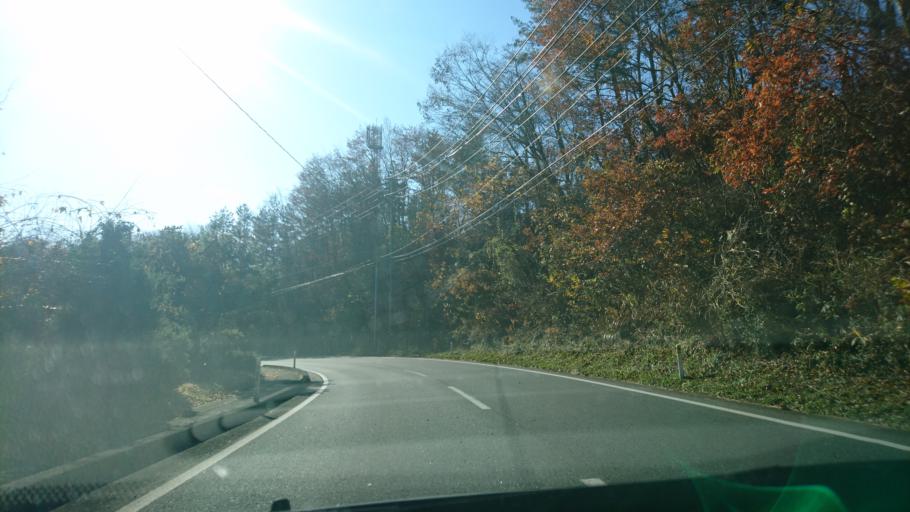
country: JP
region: Iwate
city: Ichinoseki
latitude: 38.9941
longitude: 141.2792
